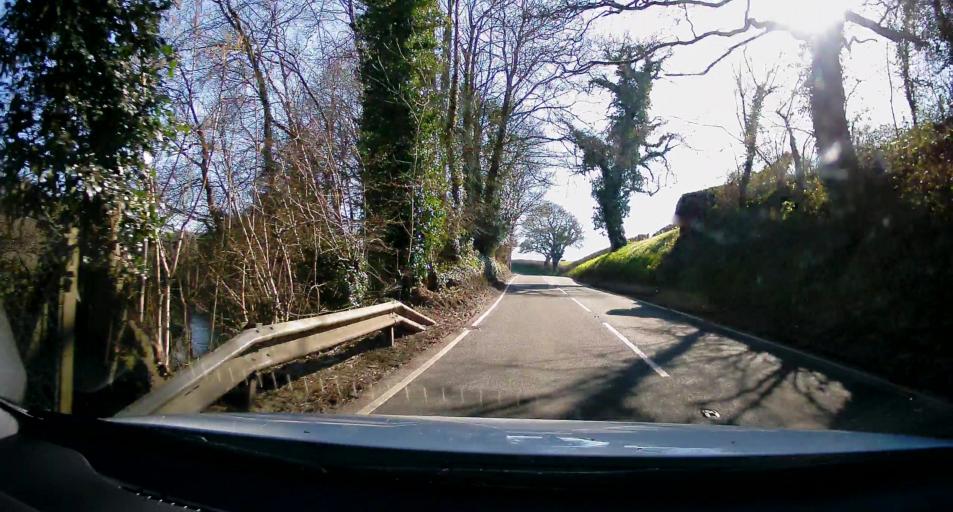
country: GB
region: Wales
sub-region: County of Ceredigion
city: Penparcau
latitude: 52.3759
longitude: -4.0725
